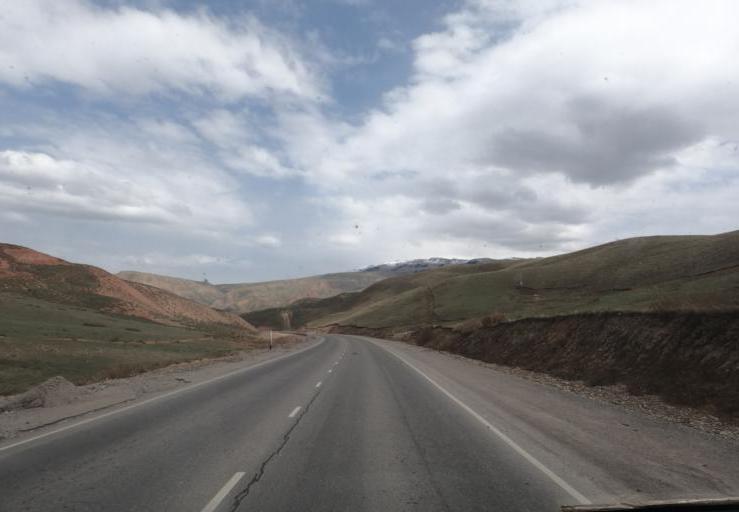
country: KG
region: Naryn
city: Naryn
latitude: 41.3805
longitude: 75.9869
